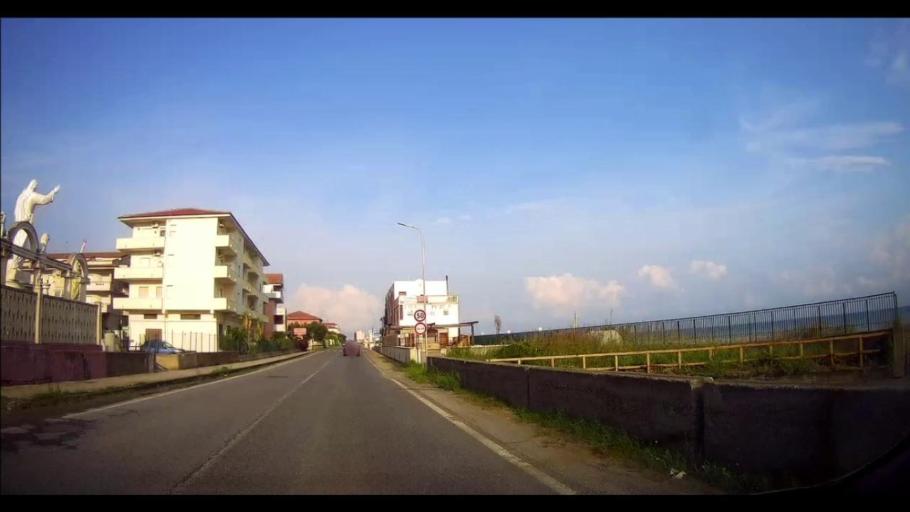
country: IT
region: Calabria
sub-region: Provincia di Cosenza
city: Cariati
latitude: 39.5090
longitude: 16.9316
